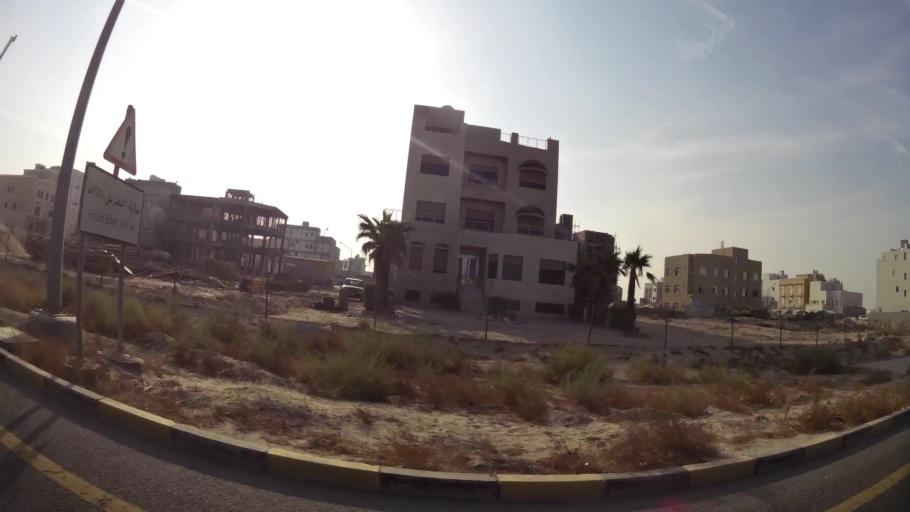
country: KW
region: Mubarak al Kabir
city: Mubarak al Kabir
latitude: 29.1996
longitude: 48.1069
